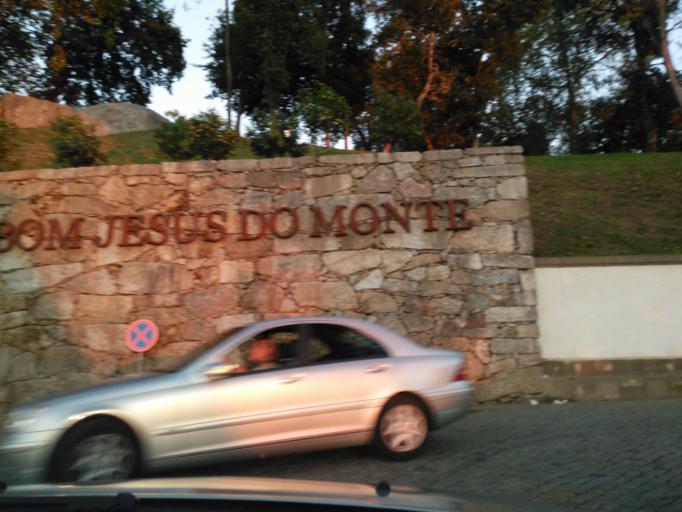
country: PT
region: Braga
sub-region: Braga
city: Adaufe
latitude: 41.5570
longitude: -8.3771
